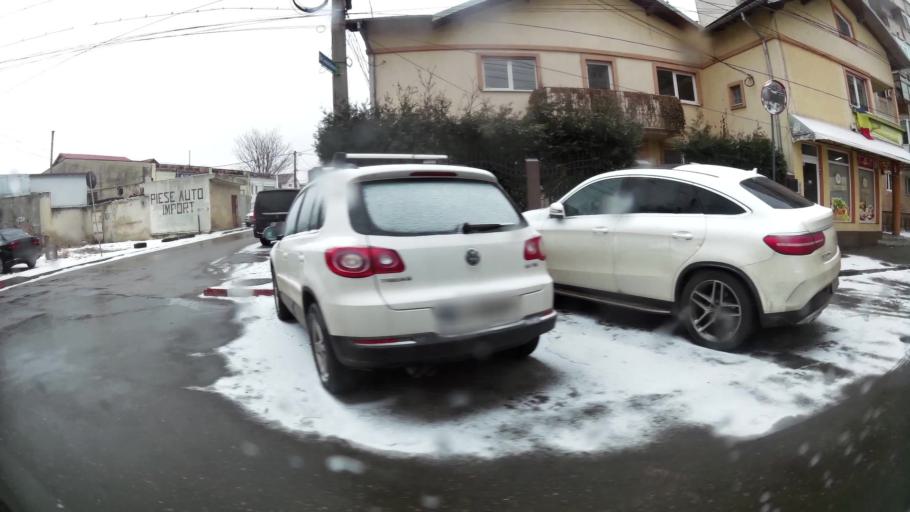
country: RO
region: Prahova
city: Ploiesti
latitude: 44.9492
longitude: 26.0099
